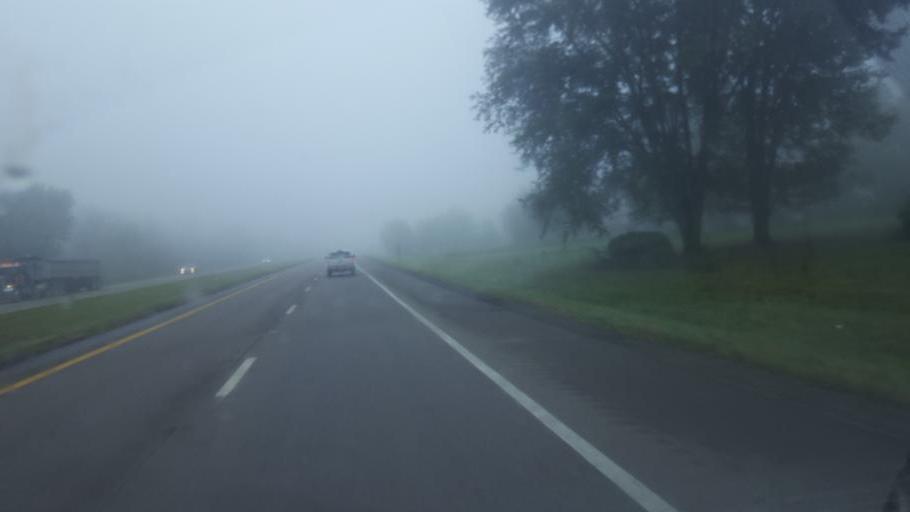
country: US
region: Ohio
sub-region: Tuscarawas County
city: New Philadelphia
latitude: 40.4870
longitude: -81.4684
